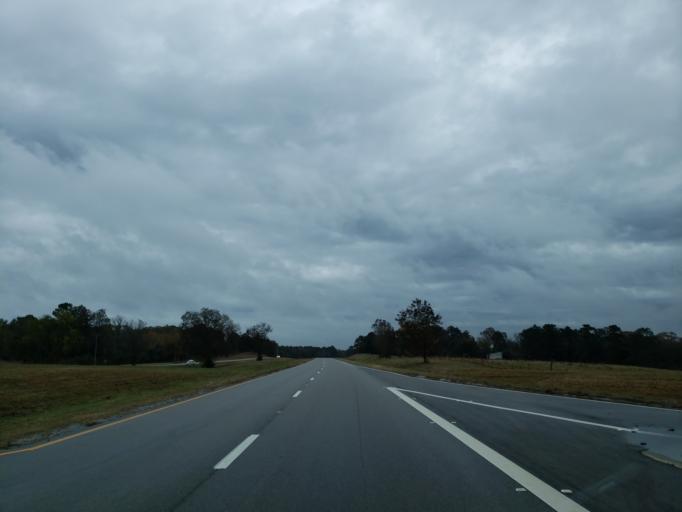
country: US
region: Mississippi
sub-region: Wayne County
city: Waynesboro
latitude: 31.6957
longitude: -88.7310
